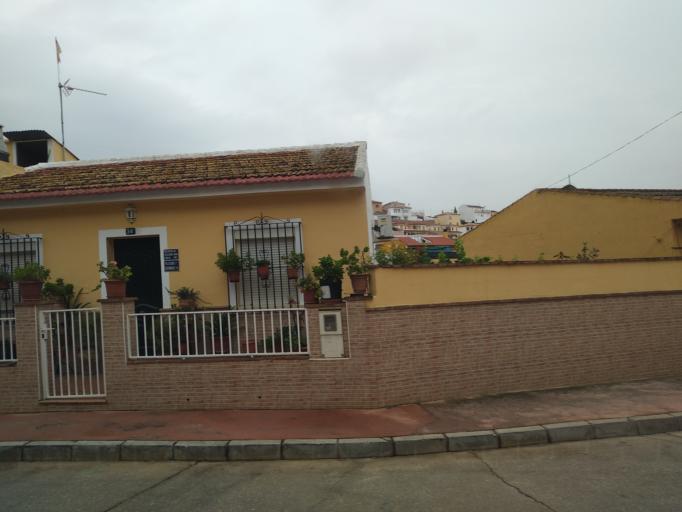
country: ES
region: Andalusia
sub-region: Provincia de Malaga
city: Malaga
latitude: 36.7470
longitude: -4.4779
